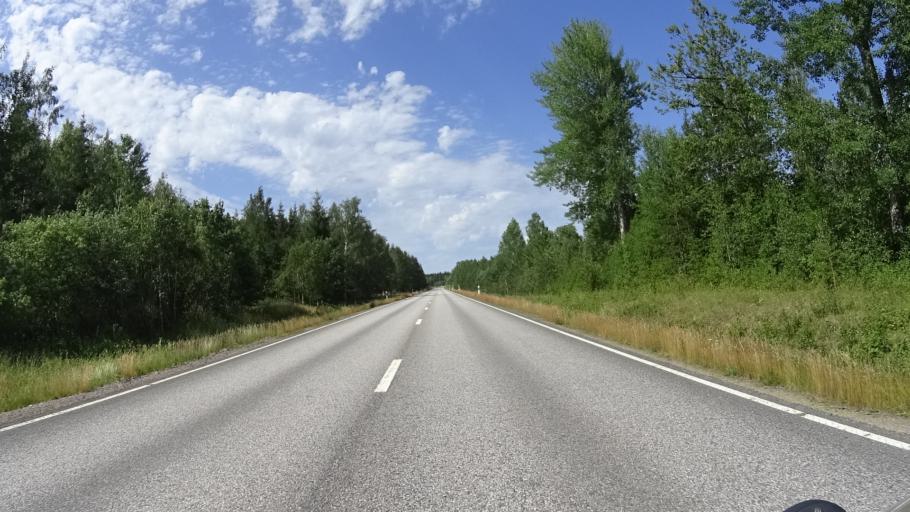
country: SE
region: Kalmar
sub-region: Vasterviks Kommun
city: Overum
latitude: 58.0619
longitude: 16.2043
